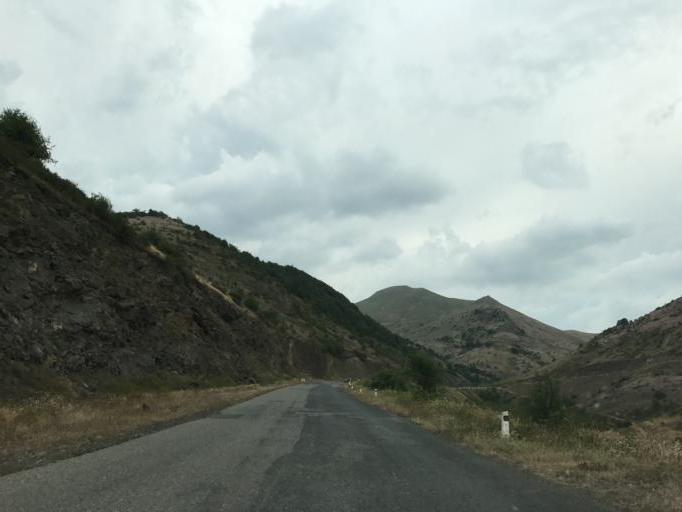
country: AZ
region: Lacin
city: Lacin
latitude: 39.6789
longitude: 46.6359
